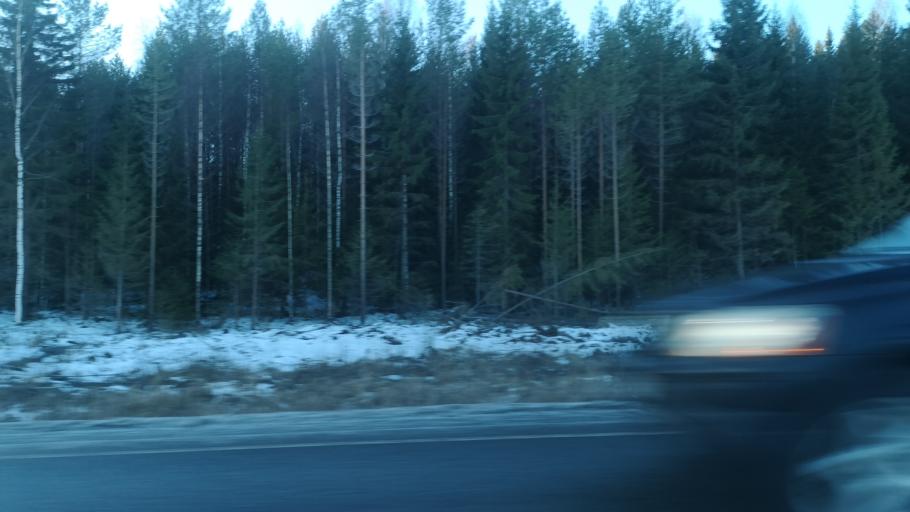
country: FI
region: Southern Savonia
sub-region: Pieksaemaeki
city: Juva
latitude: 61.7905
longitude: 27.5974
